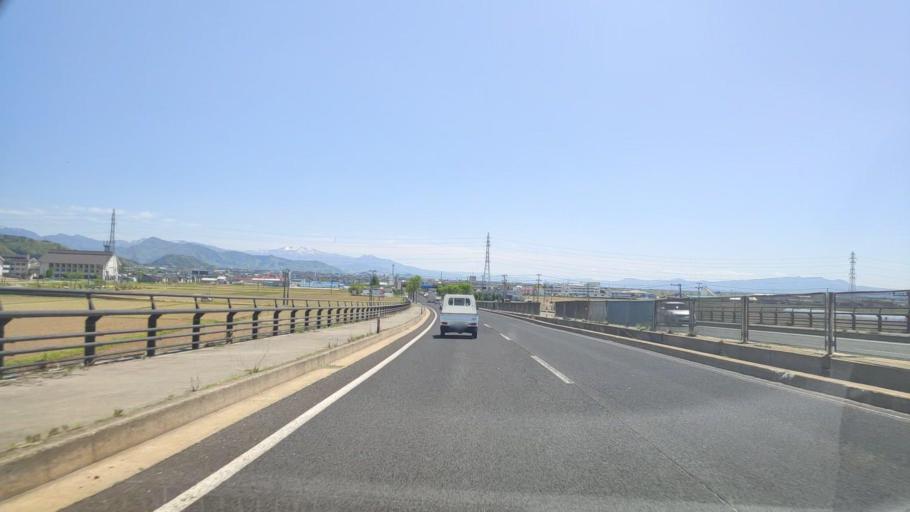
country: JP
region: Yamagata
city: Higashine
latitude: 38.4918
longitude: 140.3833
